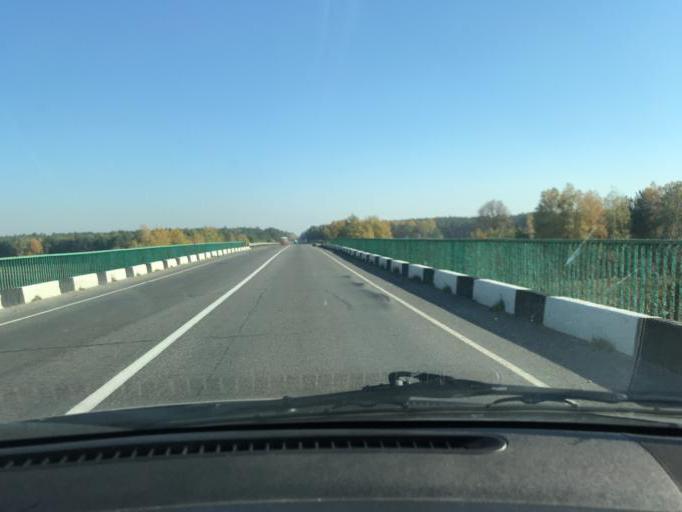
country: BY
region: Brest
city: Davyd-Haradok
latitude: 52.2360
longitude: 27.2519
